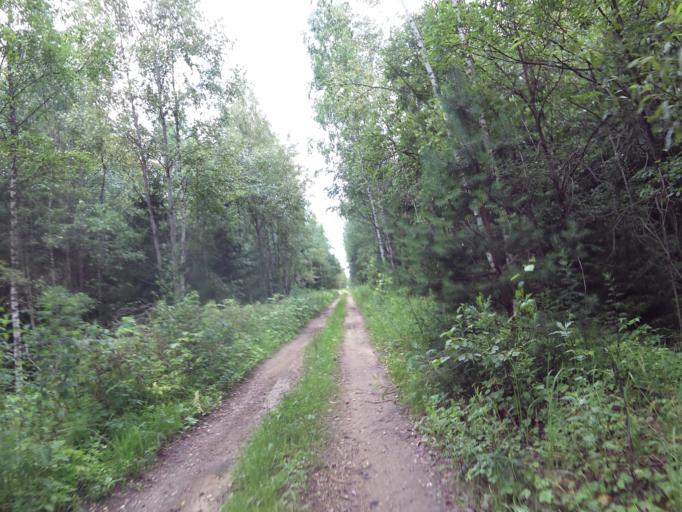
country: RU
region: Moskovskaya
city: Popovo
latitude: 54.9532
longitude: 37.7016
